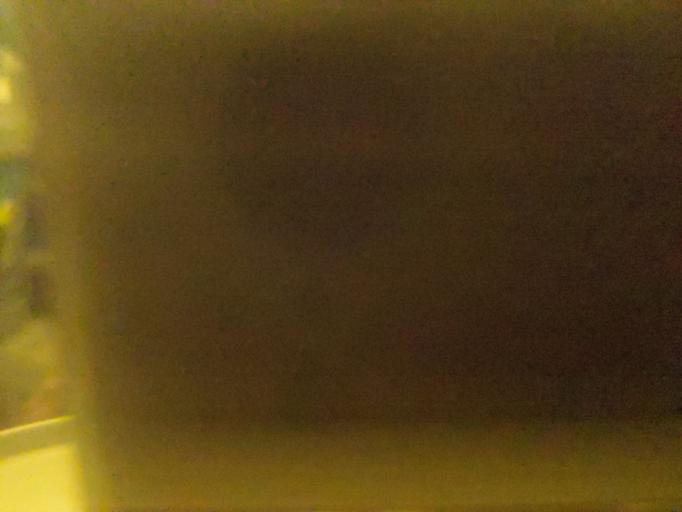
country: JP
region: Shiga Prefecture
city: Otsu-shi
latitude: 34.9773
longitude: 135.8491
